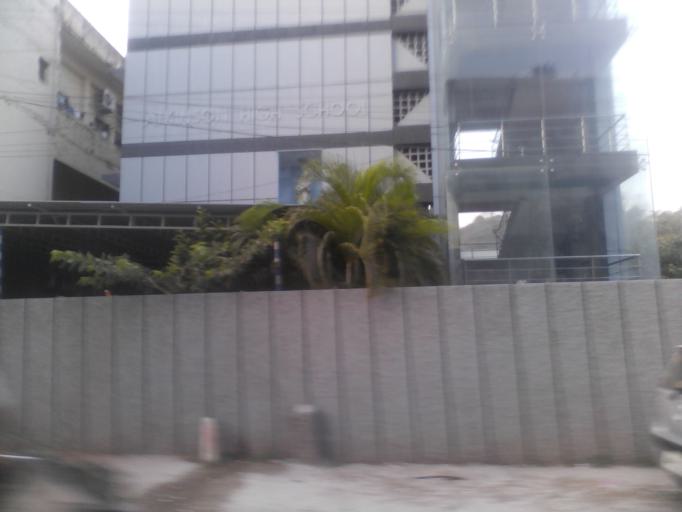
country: IN
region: Andhra Pradesh
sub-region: Krishna
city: Vijayawada
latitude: 16.5209
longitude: 80.6174
